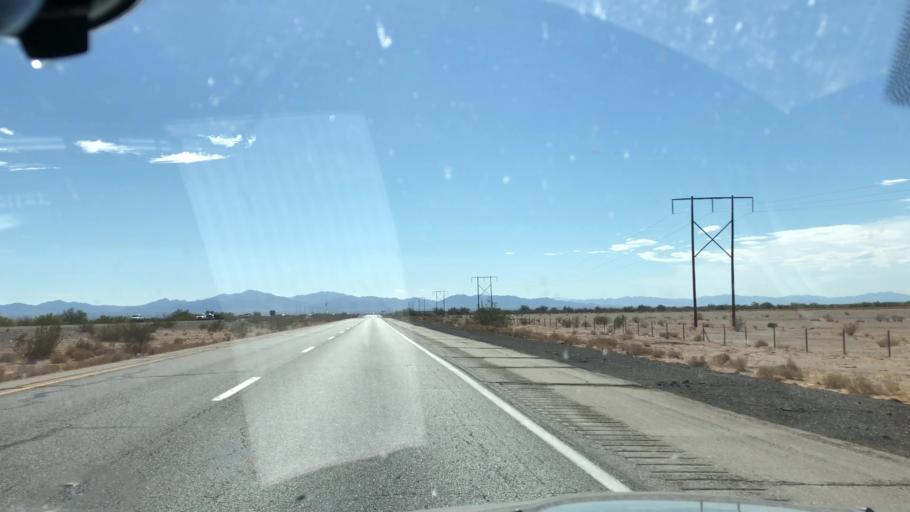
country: US
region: California
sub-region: Riverside County
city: Mesa Verde
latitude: 33.6063
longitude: -114.9650
